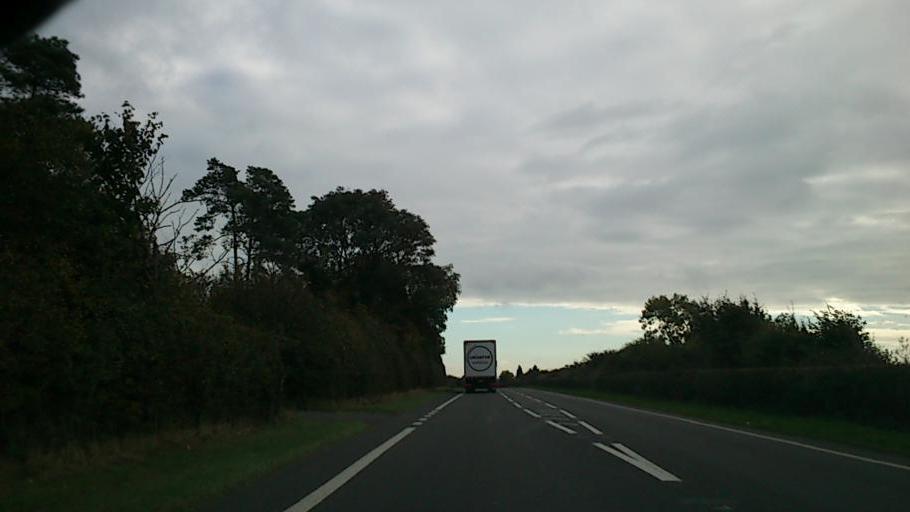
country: GB
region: England
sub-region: Shropshire
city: Westbury
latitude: 52.7064
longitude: -2.9076
